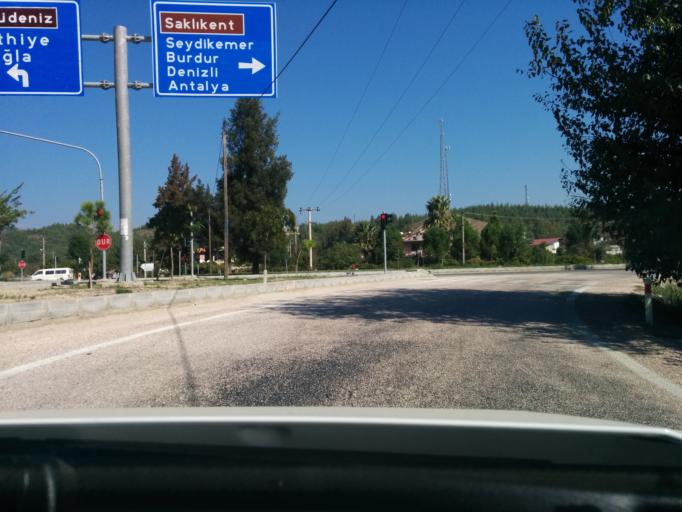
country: TR
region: Mugla
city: Kemer
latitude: 36.6329
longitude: 29.3556
